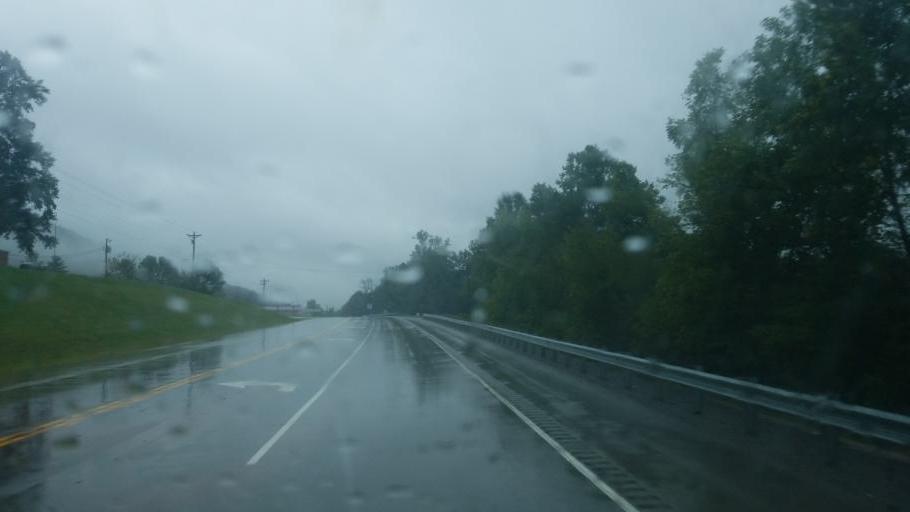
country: US
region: Kentucky
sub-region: Fleming County
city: Flemingsburg
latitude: 38.3365
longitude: -83.5955
